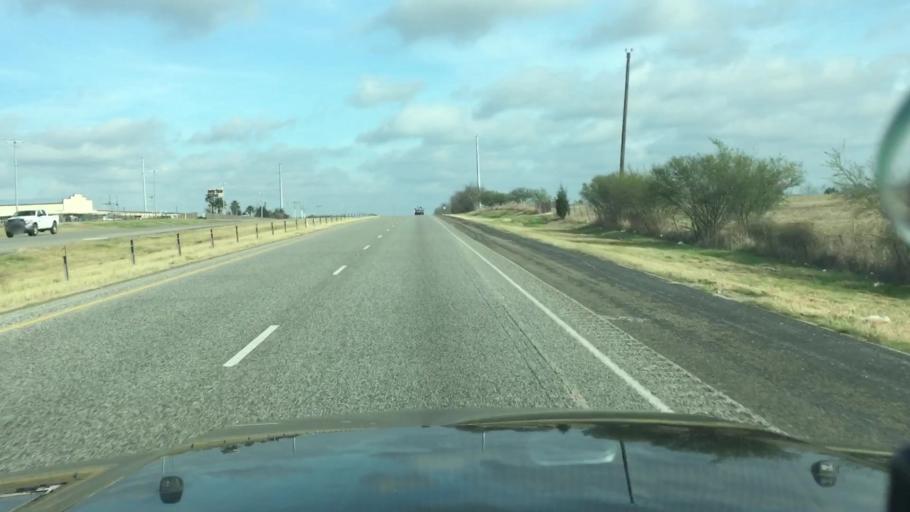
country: US
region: Texas
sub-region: Washington County
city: Brenham
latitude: 30.1370
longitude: -96.3296
